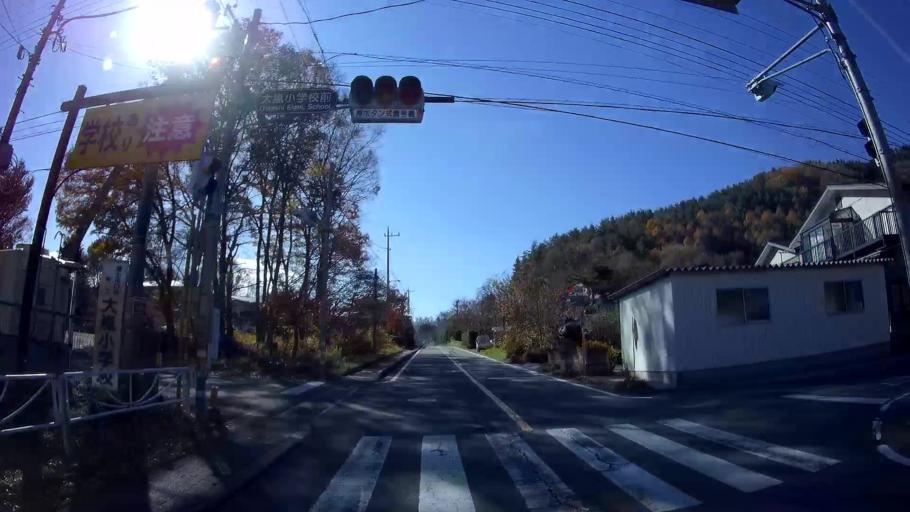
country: JP
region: Yamanashi
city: Fujikawaguchiko
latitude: 35.4961
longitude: 138.7320
